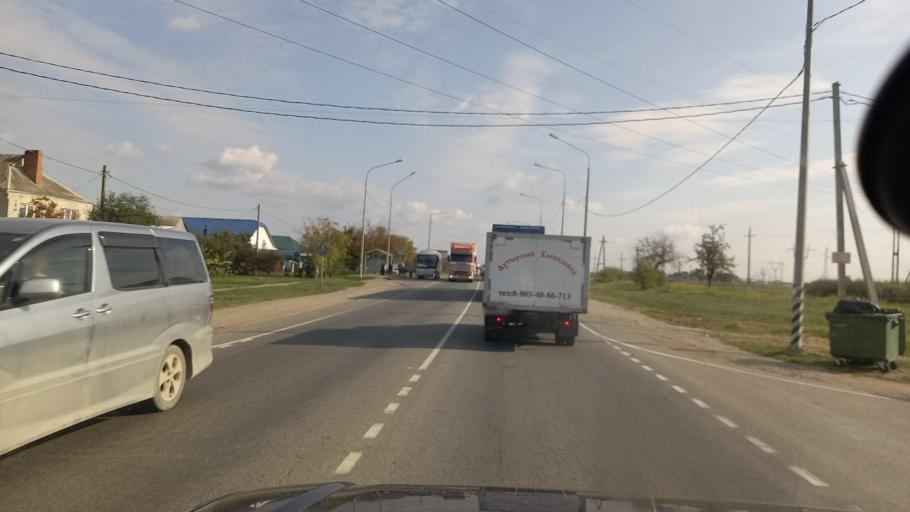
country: RU
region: Krasnodarskiy
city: Krymsk
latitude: 44.9091
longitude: 38.0035
